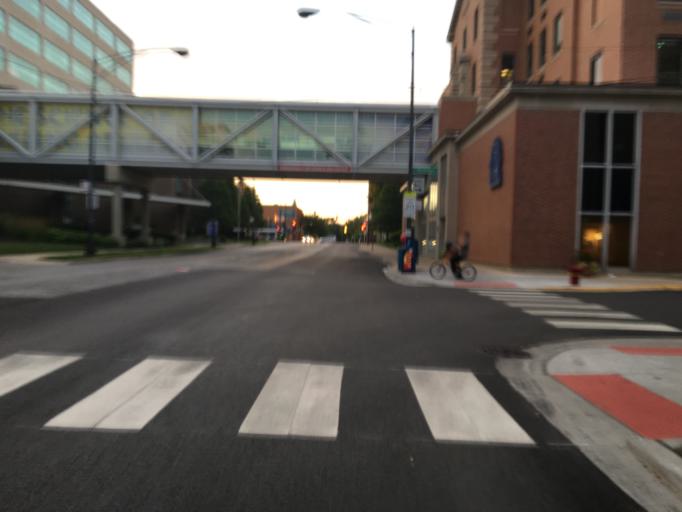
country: US
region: Illinois
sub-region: Cook County
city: Lincolnwood
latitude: 41.9747
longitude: -87.6988
